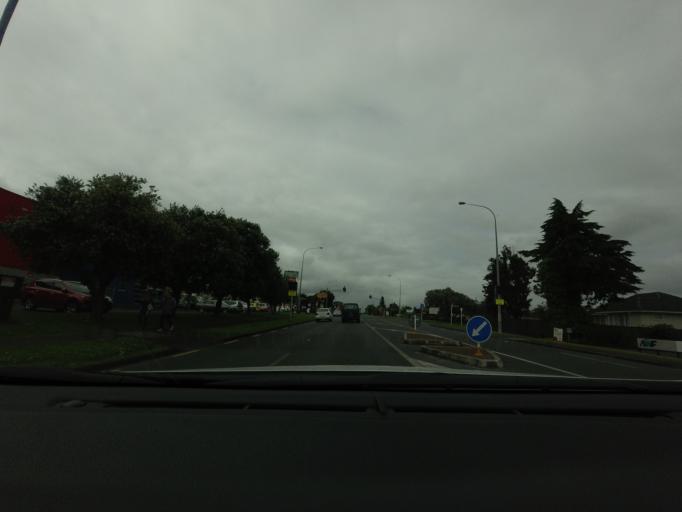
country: NZ
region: Auckland
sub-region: Auckland
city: Rosebank
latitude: -36.8651
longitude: 174.6290
